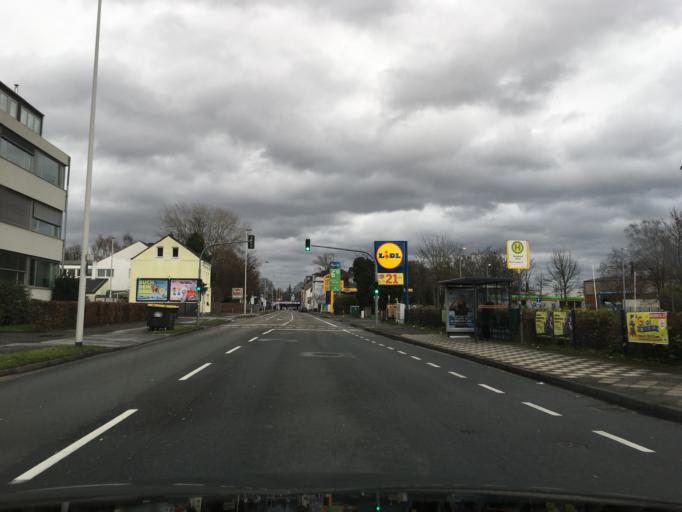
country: DE
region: North Rhine-Westphalia
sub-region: Regierungsbezirk Dusseldorf
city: Hilden
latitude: 51.1648
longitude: 6.9182
